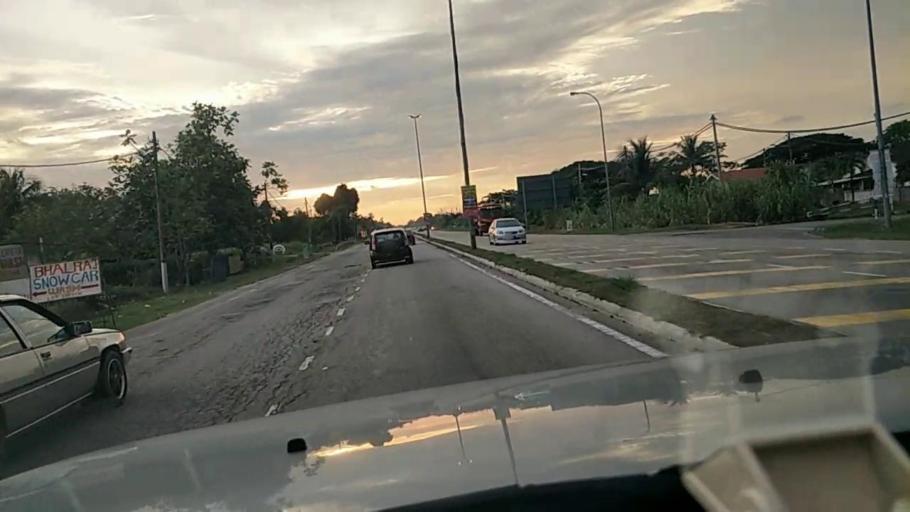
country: MY
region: Perak
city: Kampong Dungun
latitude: 3.1399
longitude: 101.3668
